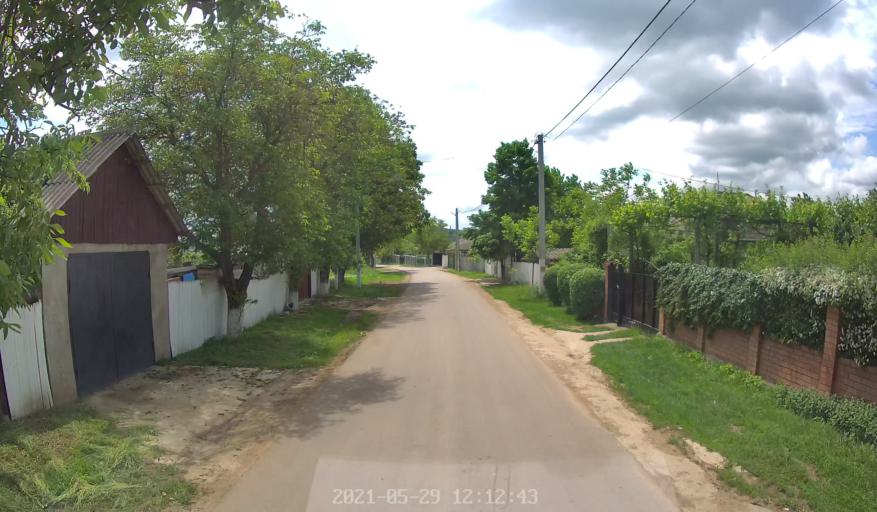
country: MD
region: Hincesti
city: Hincesti
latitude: 46.8781
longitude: 28.6321
